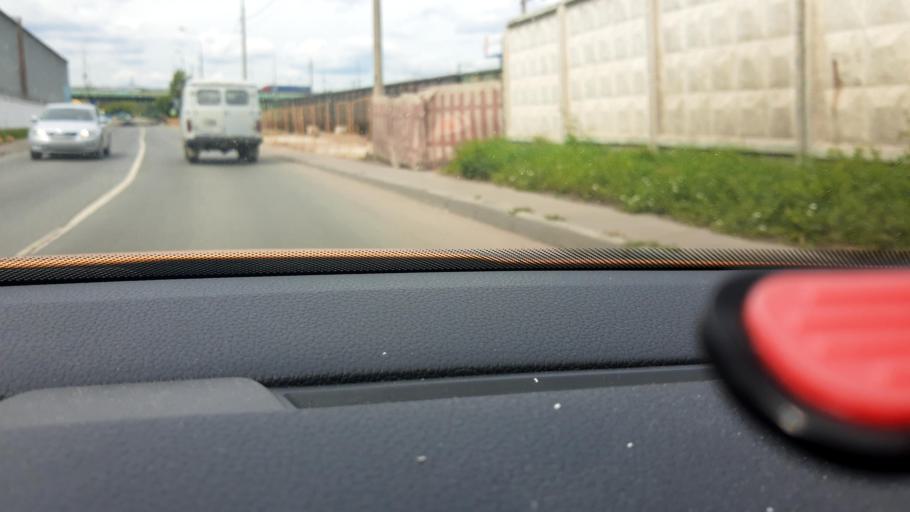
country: RU
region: Moskovskaya
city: Reutov
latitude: 55.7793
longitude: 37.8628
